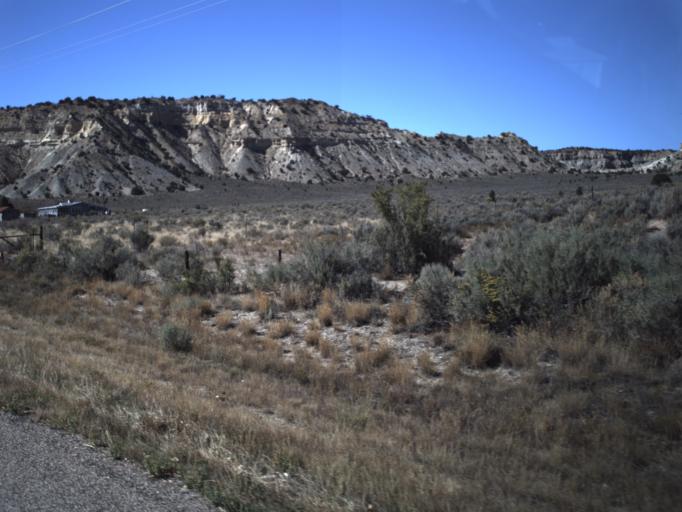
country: US
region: Utah
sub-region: Garfield County
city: Panguitch
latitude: 37.5627
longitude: -112.0078
